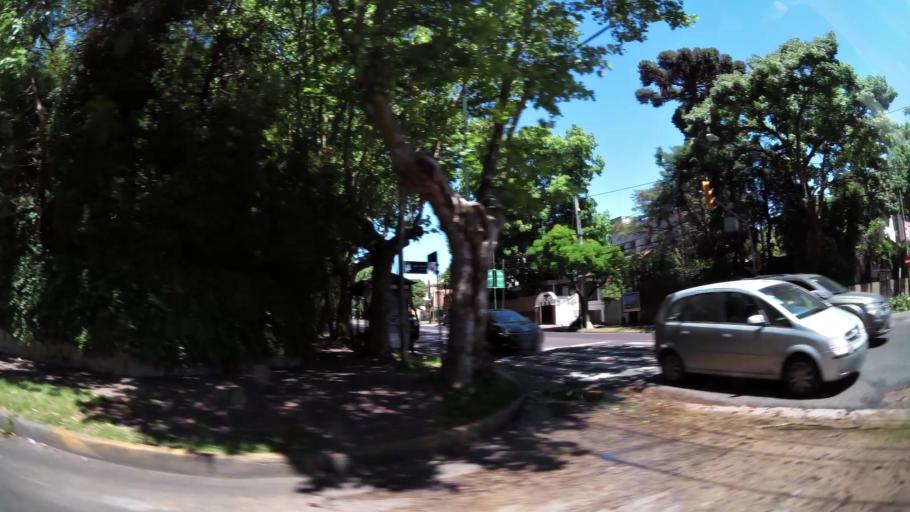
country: AR
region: Buenos Aires
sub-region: Partido de San Isidro
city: San Isidro
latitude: -34.4581
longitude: -58.5209
